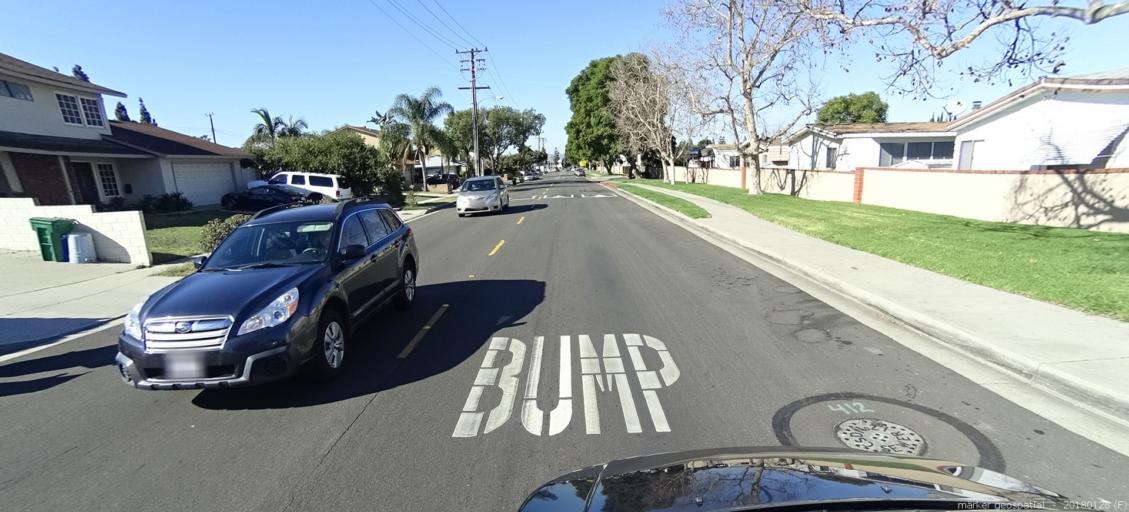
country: US
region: California
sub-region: Los Angeles County
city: Walnut
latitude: 34.0029
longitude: -117.8505
